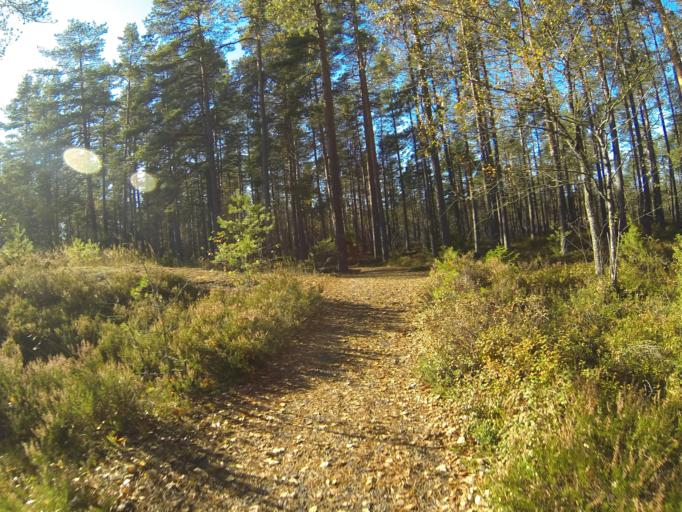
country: FI
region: Varsinais-Suomi
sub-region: Salo
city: Saerkisalo
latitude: 60.2058
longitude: 22.9394
